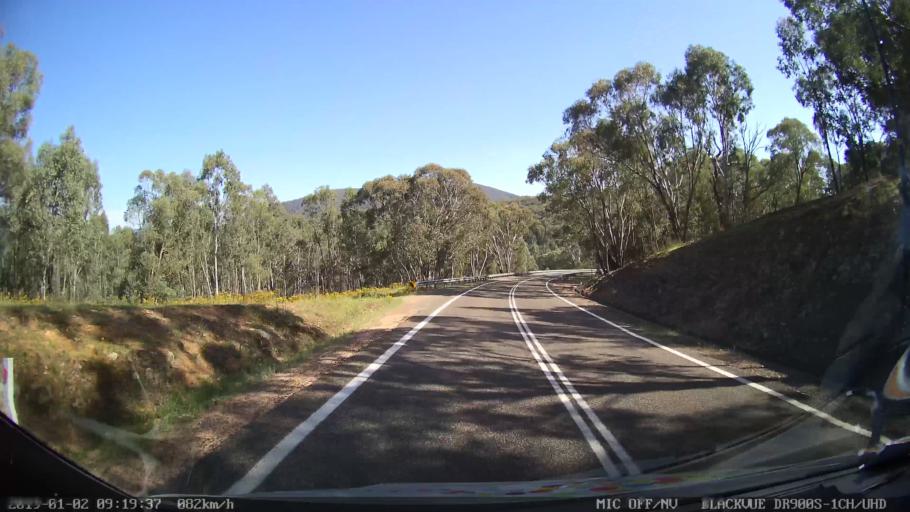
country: AU
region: New South Wales
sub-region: Tumut Shire
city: Tumut
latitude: -35.4204
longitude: 148.2767
